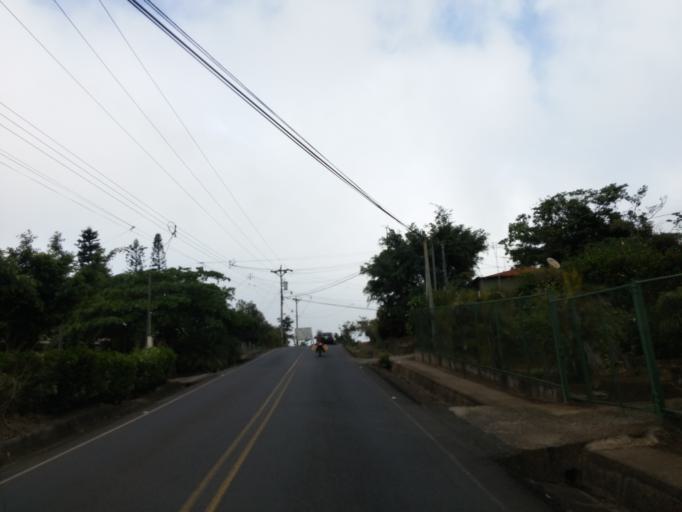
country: CR
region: Alajuela
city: San Ramon
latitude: 10.1278
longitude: -84.4725
